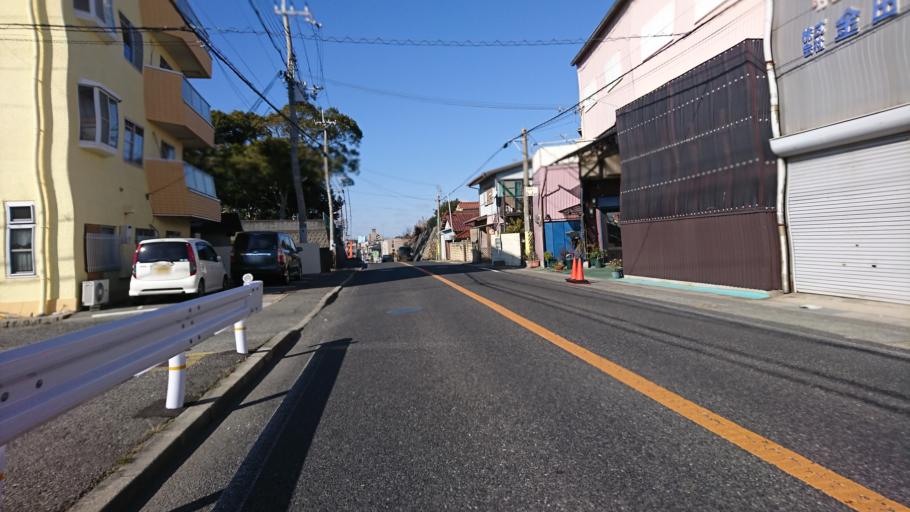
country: JP
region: Hyogo
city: Akashi
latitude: 34.6649
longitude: 134.9448
